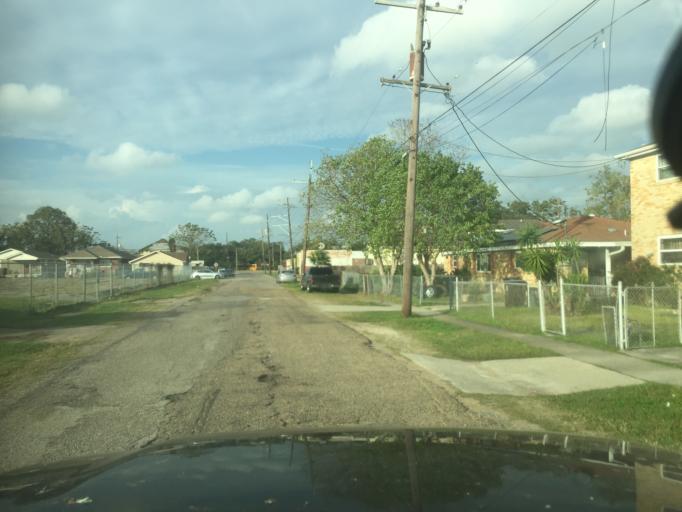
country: US
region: Louisiana
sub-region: Orleans Parish
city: New Orleans
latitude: 29.9949
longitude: -90.0794
